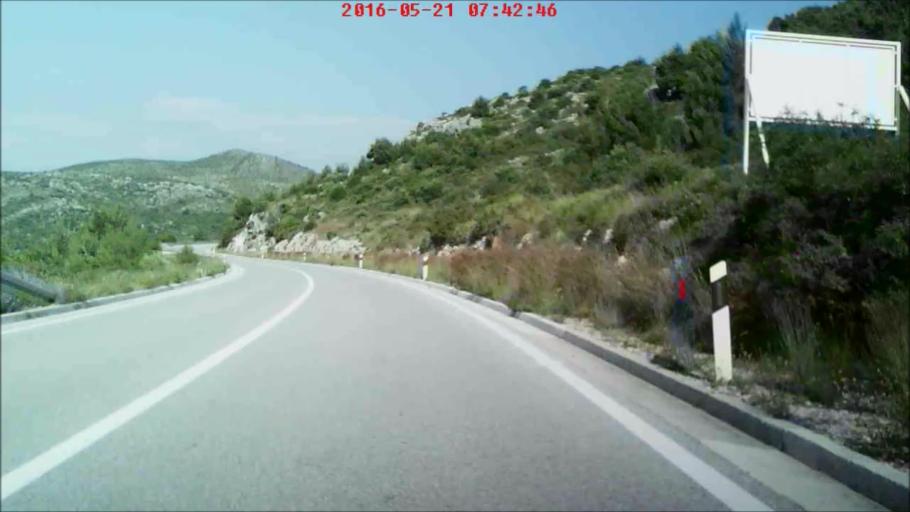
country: HR
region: Dubrovacko-Neretvanska
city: Podgora
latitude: 42.8110
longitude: 17.7987
